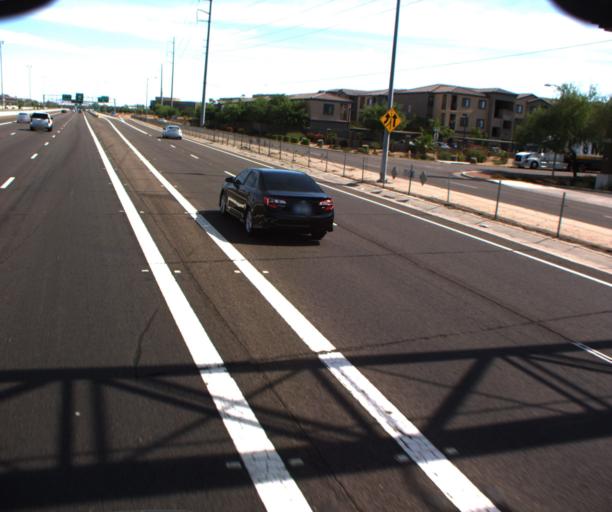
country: US
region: Arizona
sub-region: Maricopa County
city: Glendale
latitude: 33.6501
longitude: -112.1147
